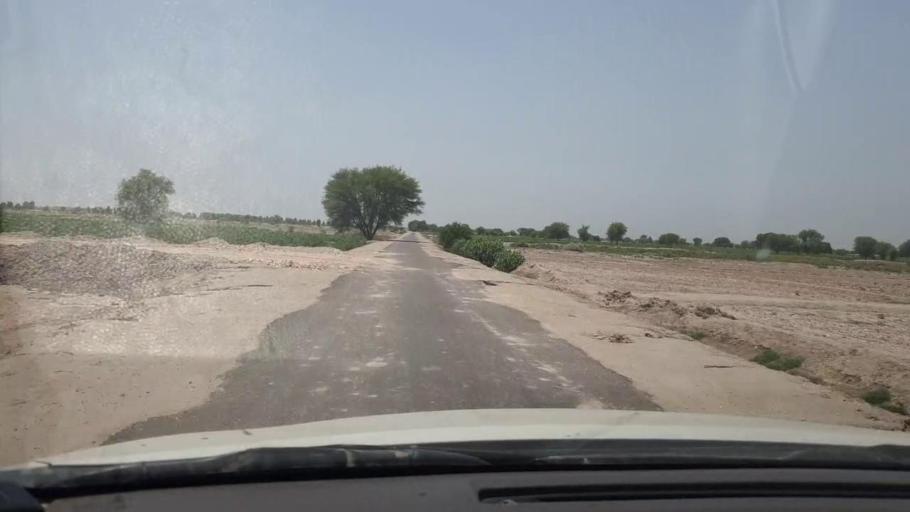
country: PK
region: Sindh
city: Rohri
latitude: 27.5208
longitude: 69.1733
